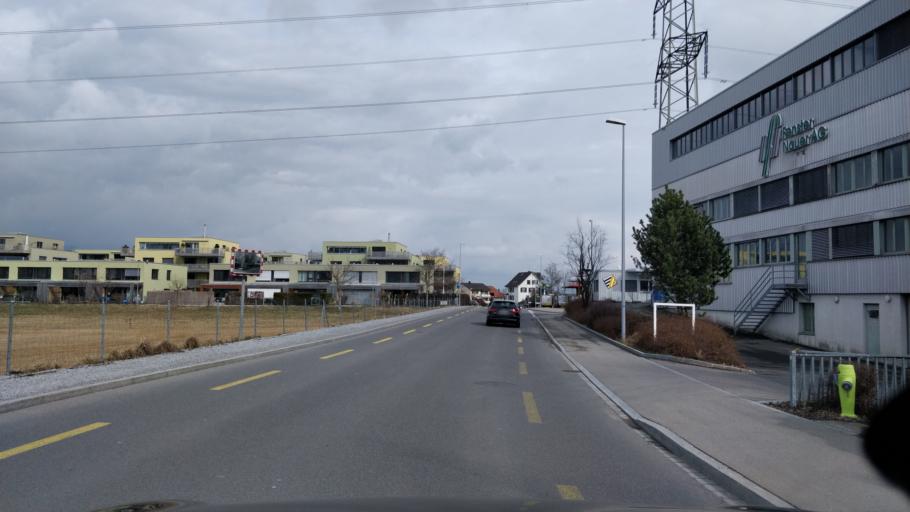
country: CH
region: Zurich
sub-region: Bezirk Horgen
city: Richterswil / Burghalde
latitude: 47.1908
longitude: 8.6784
